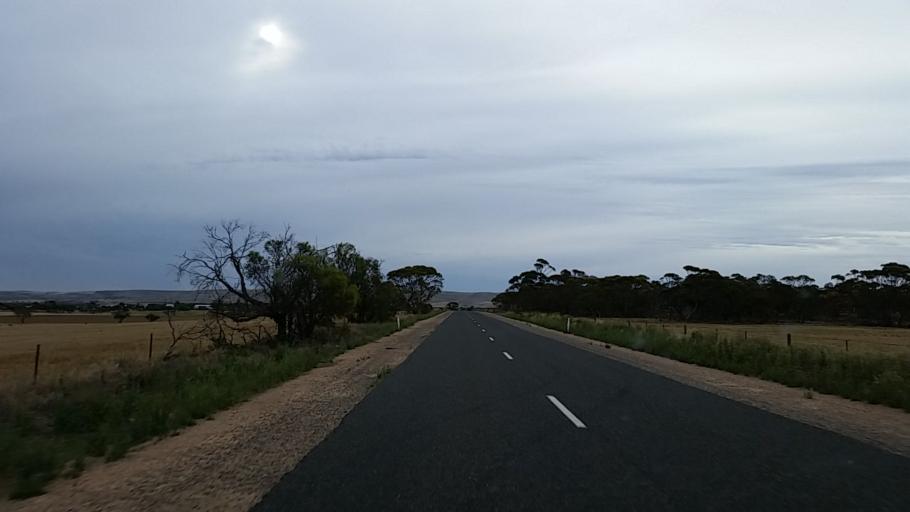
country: AU
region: South Australia
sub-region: Mid Murray
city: Mannum
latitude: -34.7554
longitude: 139.2754
